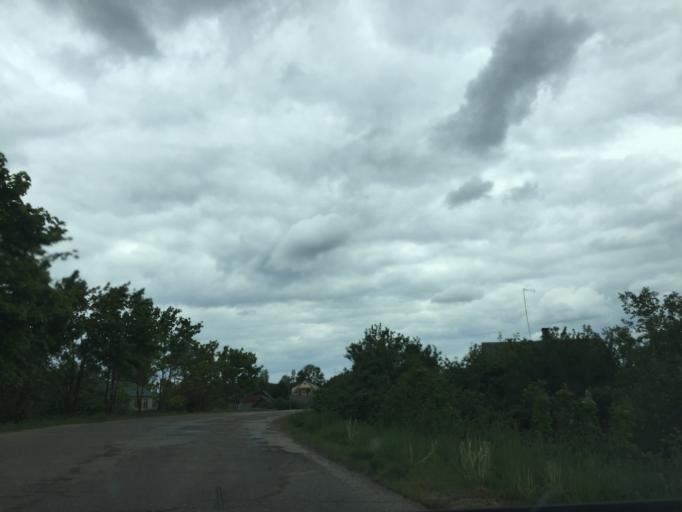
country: LV
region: Dagda
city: Dagda
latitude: 56.0850
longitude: 27.5313
